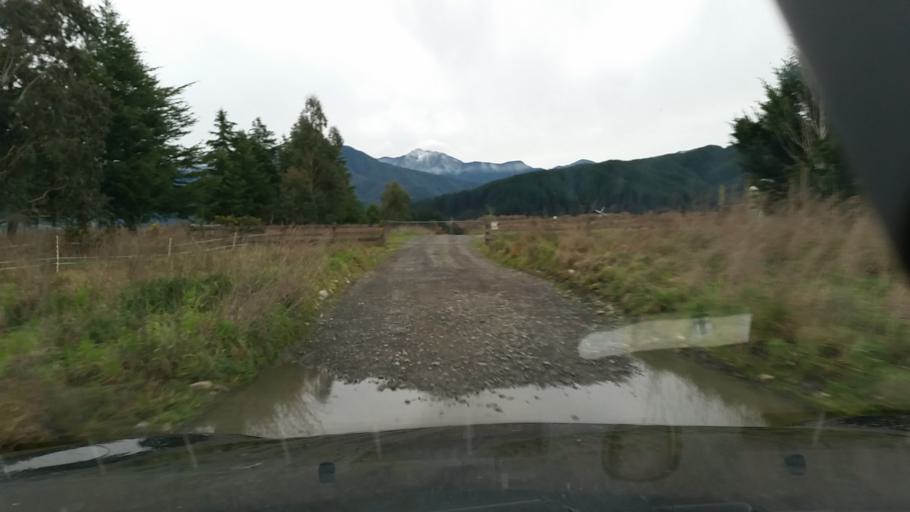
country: NZ
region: Marlborough
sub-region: Marlborough District
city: Blenheim
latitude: -41.5345
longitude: 173.6128
